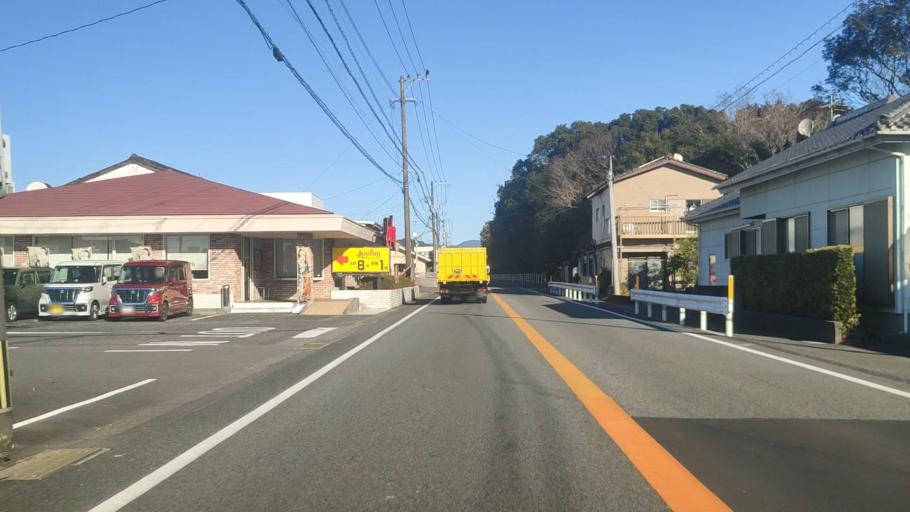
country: JP
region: Miyazaki
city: Nobeoka
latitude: 32.5258
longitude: 131.6826
